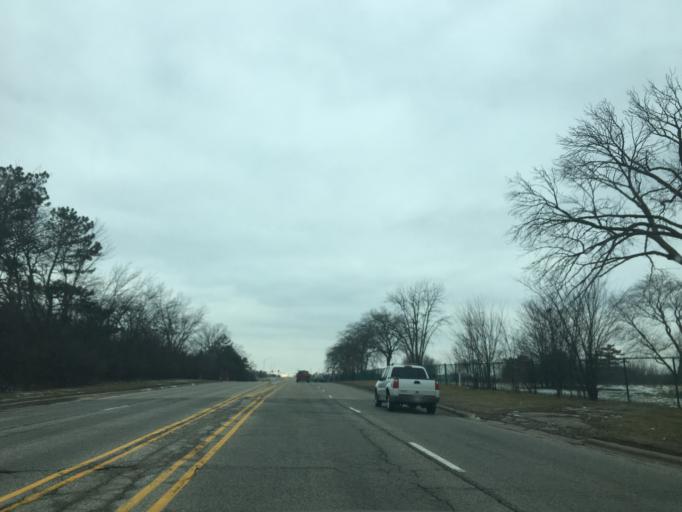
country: US
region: Illinois
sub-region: DuPage County
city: Oak Brook
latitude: 41.8479
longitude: -87.9127
